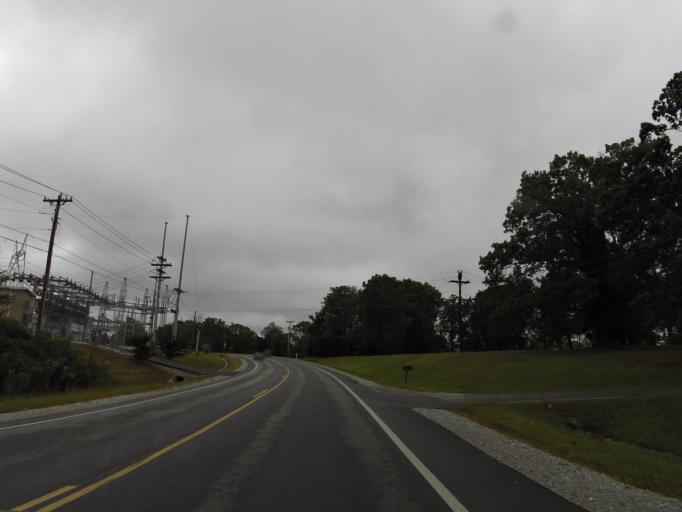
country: US
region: Tennessee
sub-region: Hamilton County
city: Collegedale
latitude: 35.1220
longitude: -85.0471
